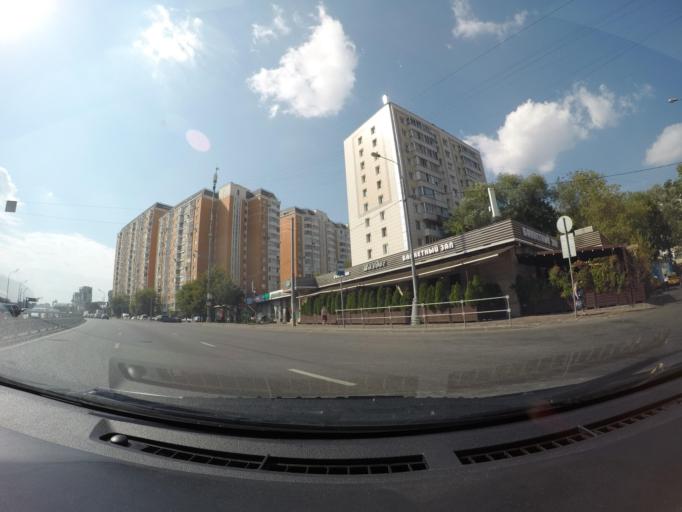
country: RU
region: Moscow
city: Zapadnoye Degunino
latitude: 55.8737
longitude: 37.5210
